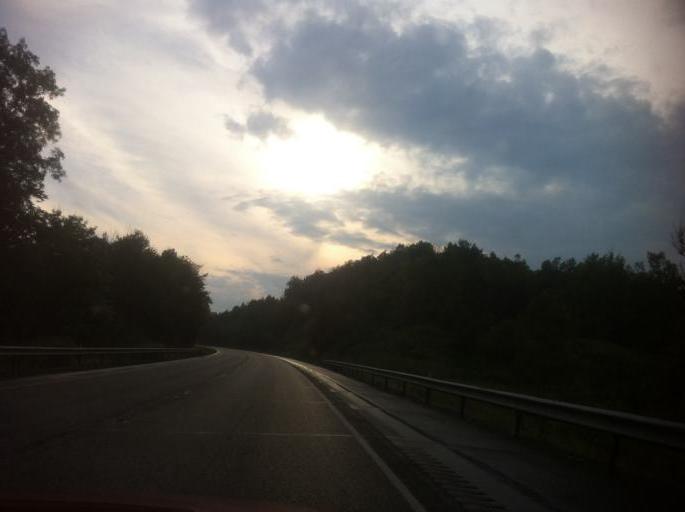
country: US
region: Pennsylvania
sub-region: Clarion County
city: Knox
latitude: 41.1983
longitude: -79.6280
